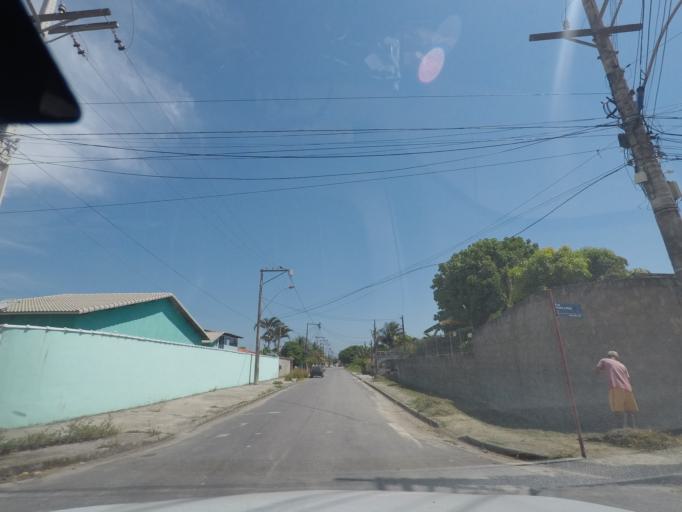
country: BR
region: Rio de Janeiro
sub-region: Marica
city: Marica
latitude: -22.9594
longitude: -42.9595
